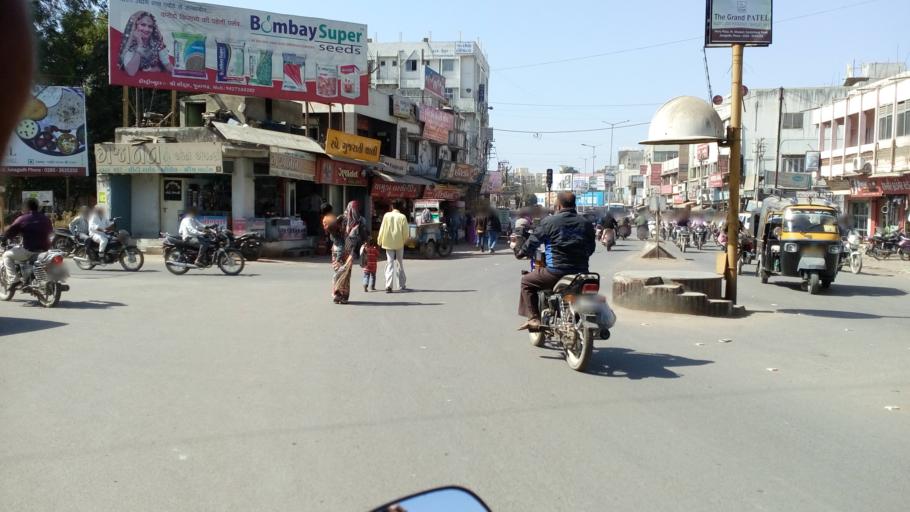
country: IN
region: Gujarat
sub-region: Junagadh
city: Junagadh
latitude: 21.5150
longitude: 70.4614
